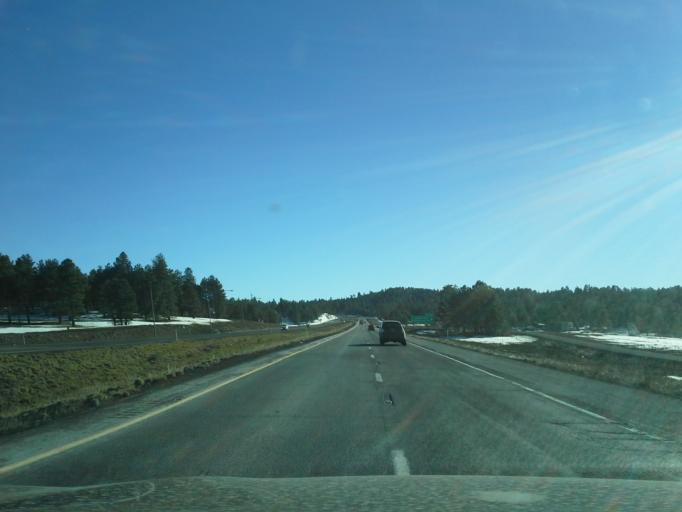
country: US
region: Arizona
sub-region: Coconino County
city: Kachina Village
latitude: 35.0964
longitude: -111.6840
